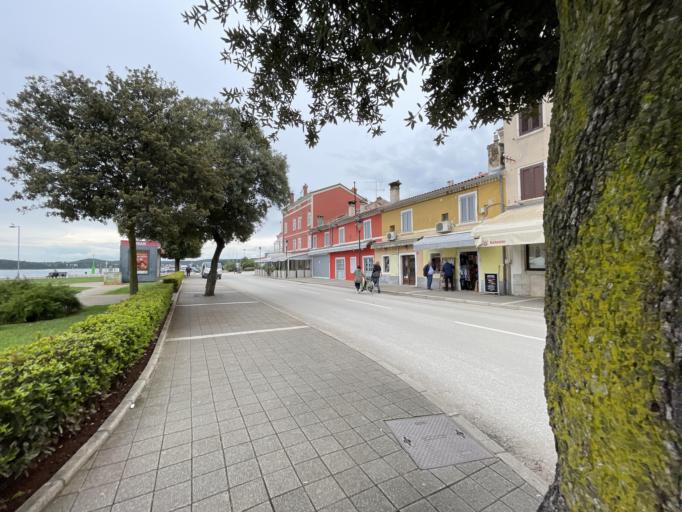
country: HR
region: Istarska
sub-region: Grad Rovinj
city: Rovinj
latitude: 45.0837
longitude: 13.6343
